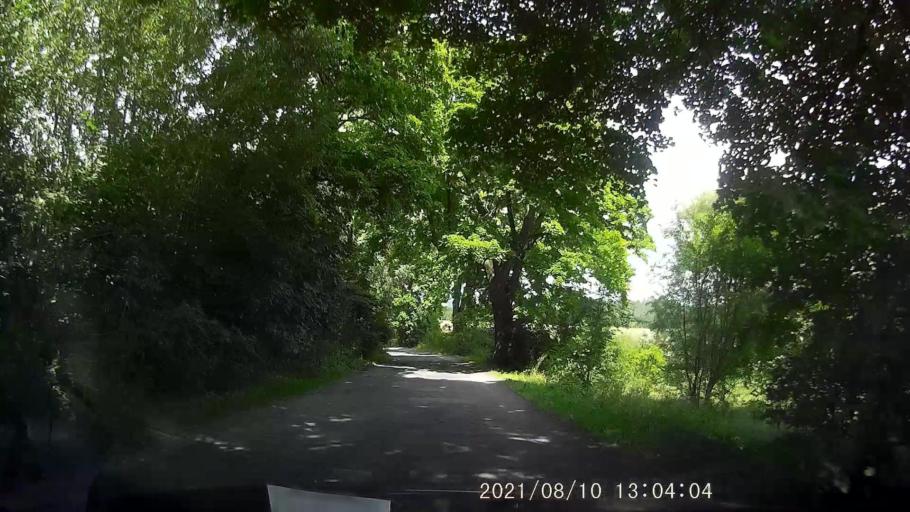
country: PL
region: Lower Silesian Voivodeship
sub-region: Powiat klodzki
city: Bozkow
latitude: 50.4745
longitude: 16.5646
